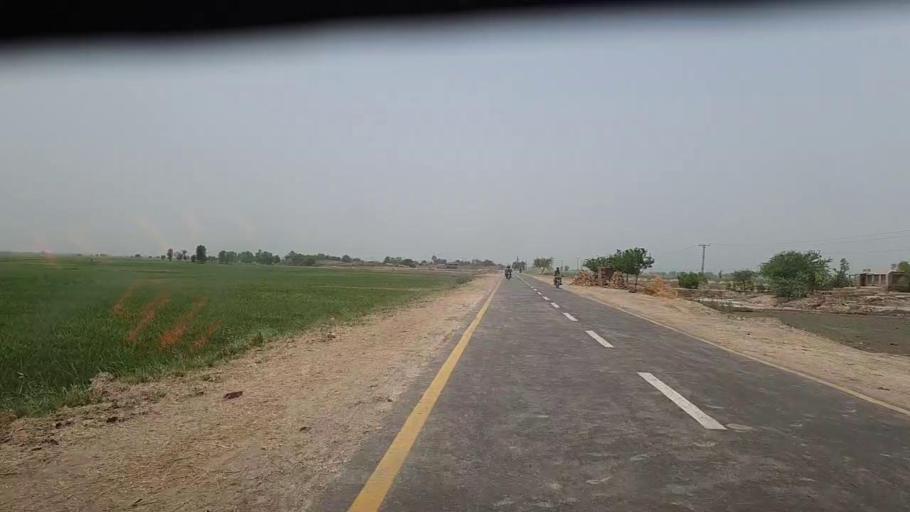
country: PK
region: Sindh
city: Sita Road
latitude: 27.0403
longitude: 67.8883
